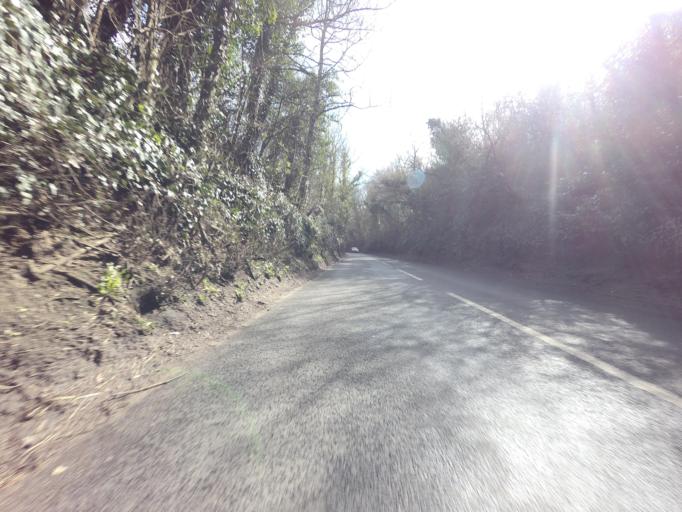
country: GB
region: England
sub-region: Greater London
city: Orpington
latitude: 51.3864
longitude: 0.1335
